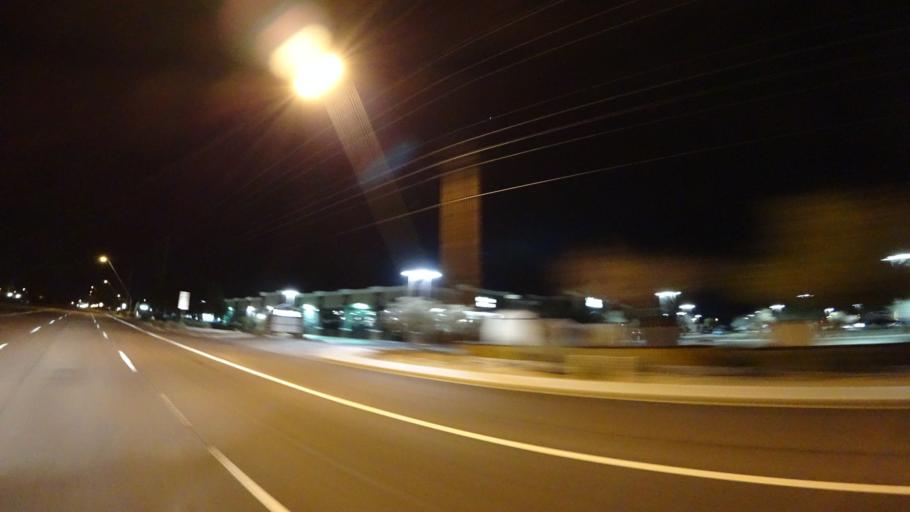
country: US
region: Arizona
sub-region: Pinal County
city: Apache Junction
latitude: 33.3933
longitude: -111.6310
